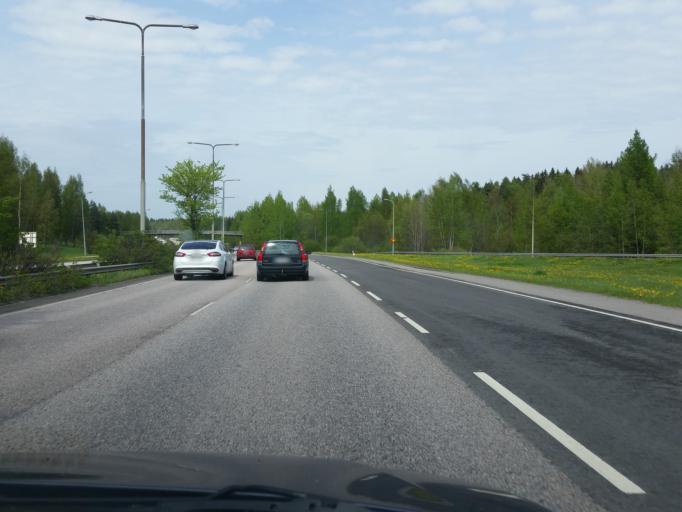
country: FI
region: Uusimaa
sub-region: Helsinki
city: Helsinki
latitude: 60.2205
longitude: 24.9096
